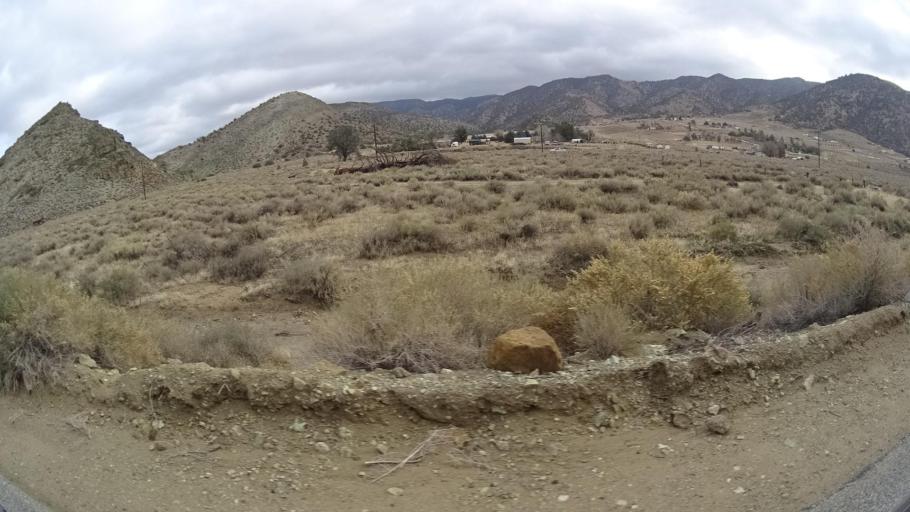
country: US
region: California
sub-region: Kern County
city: Tehachapi
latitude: 35.1485
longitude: -118.3125
